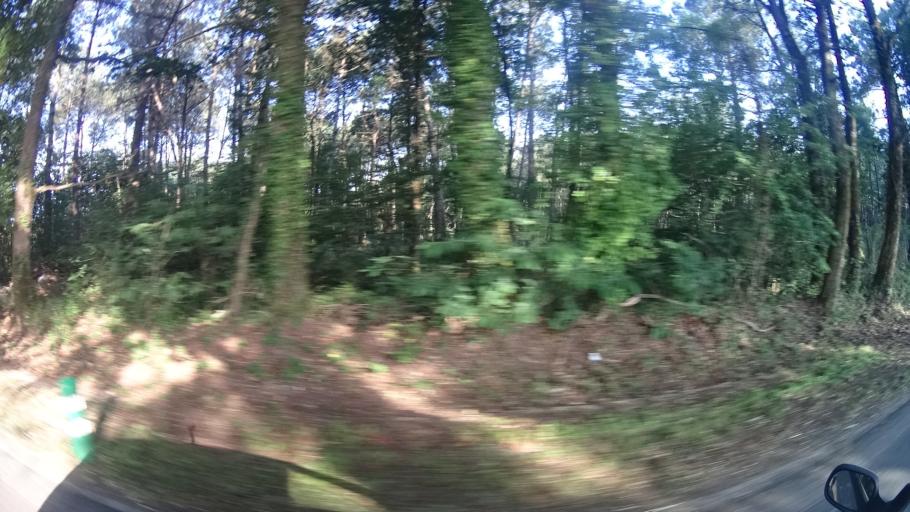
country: FR
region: Brittany
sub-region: Departement d'Ille-et-Vilaine
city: Bains-sur-Oust
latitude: 47.6888
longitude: -2.0616
